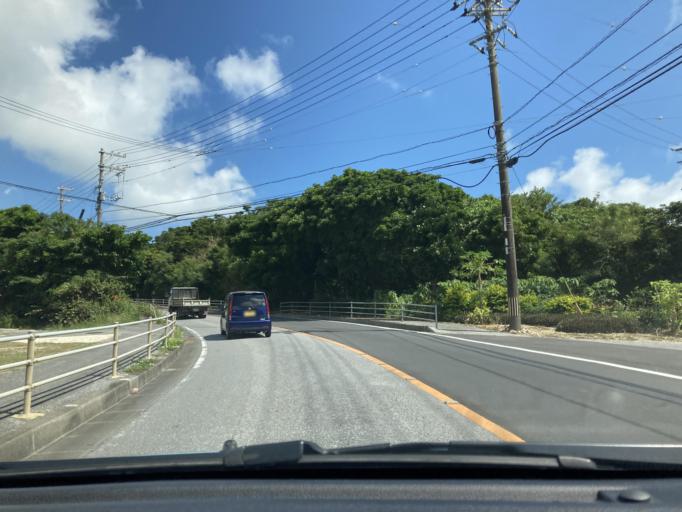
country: JP
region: Okinawa
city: Tomigusuku
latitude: 26.1532
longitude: 127.7804
